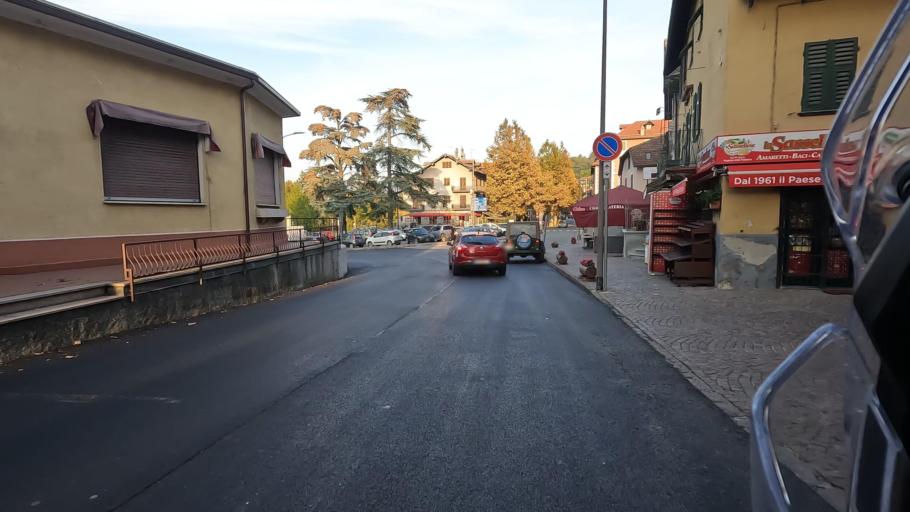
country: IT
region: Liguria
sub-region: Provincia di Savona
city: Sassello
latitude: 44.4793
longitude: 8.4898
